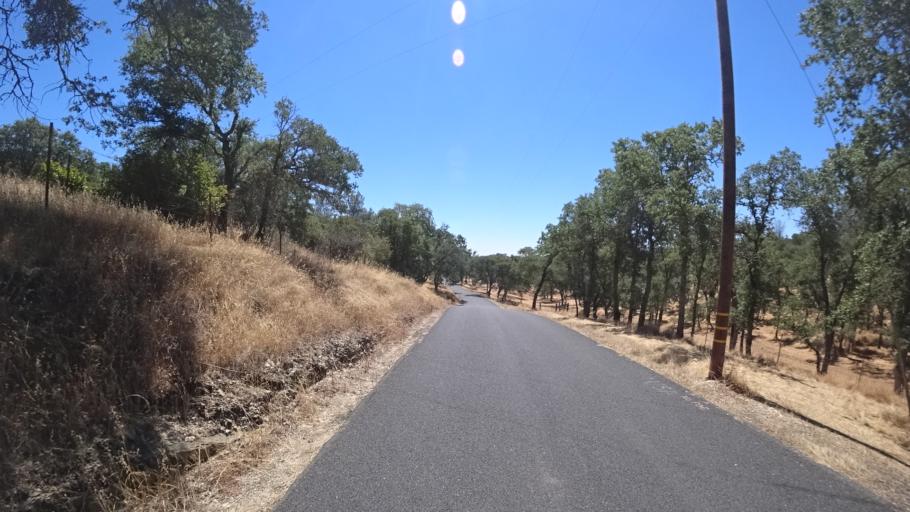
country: US
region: California
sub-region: Calaveras County
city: Copperopolis
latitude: 37.9663
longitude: -120.6899
